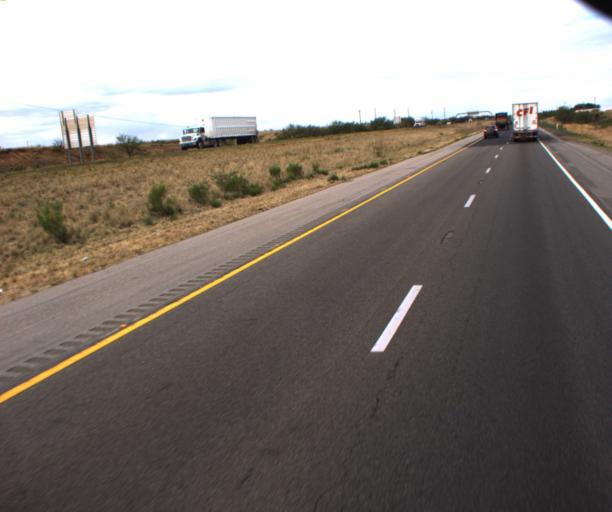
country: US
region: Arizona
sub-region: Cochise County
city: Whetstone
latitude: 31.9634
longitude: -110.3710
